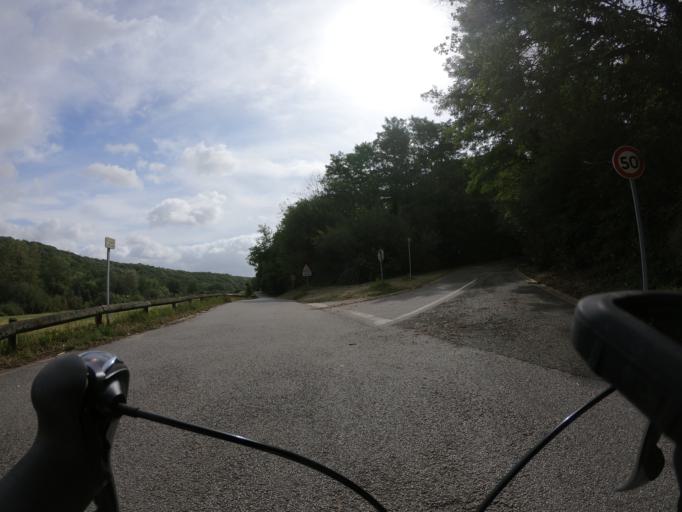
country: FR
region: Ile-de-France
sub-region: Departement des Yvelines
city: Voisins-le-Bretonneux
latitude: 48.7478
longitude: 2.0505
